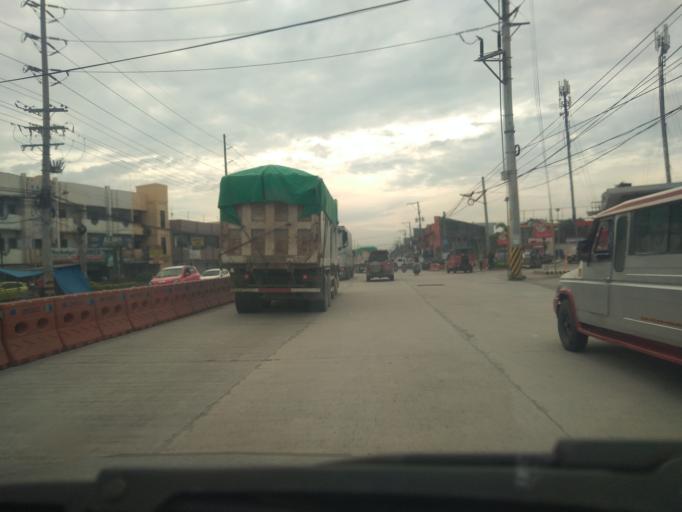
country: PH
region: Central Luzon
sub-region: Province of Pampanga
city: Magliman
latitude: 15.0452
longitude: 120.6720
